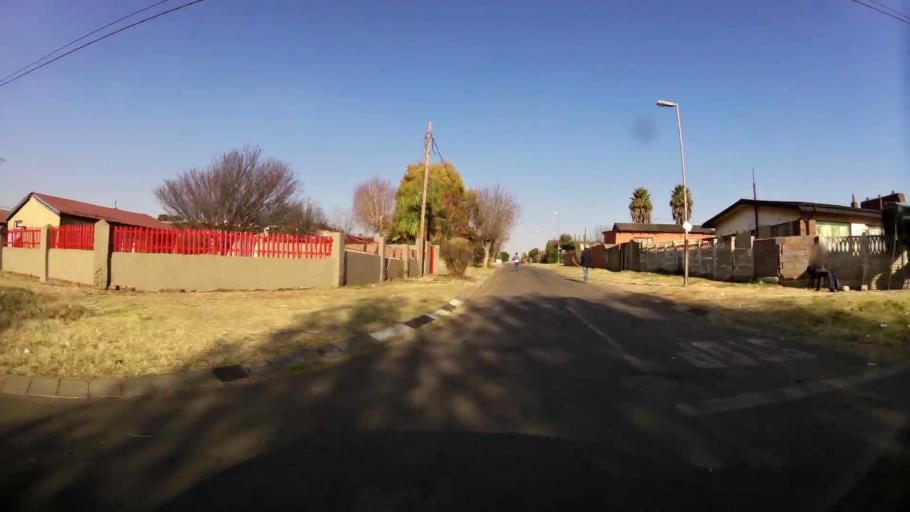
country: ZA
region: Gauteng
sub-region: City of Johannesburg Metropolitan Municipality
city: Soweto
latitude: -26.2645
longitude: 27.8697
